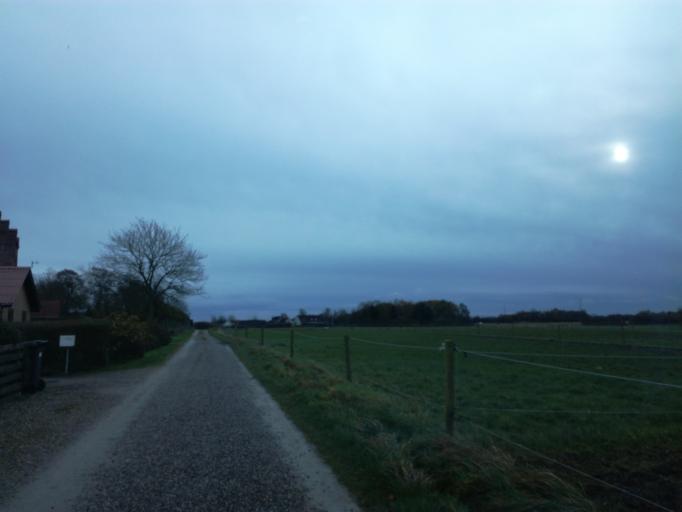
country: DK
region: South Denmark
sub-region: Vejle Kommune
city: Brejning
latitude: 55.6368
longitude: 9.6916
